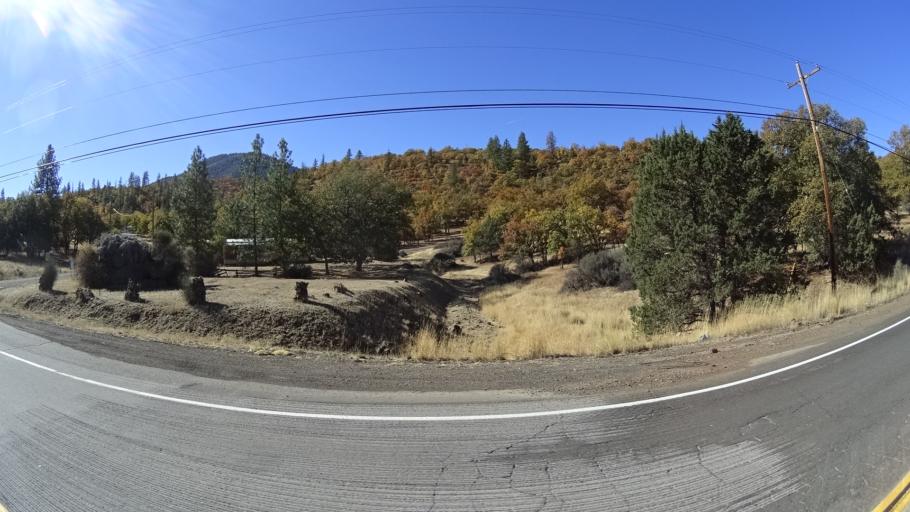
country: US
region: California
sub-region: Siskiyou County
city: Montague
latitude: 41.8925
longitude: -122.5014
